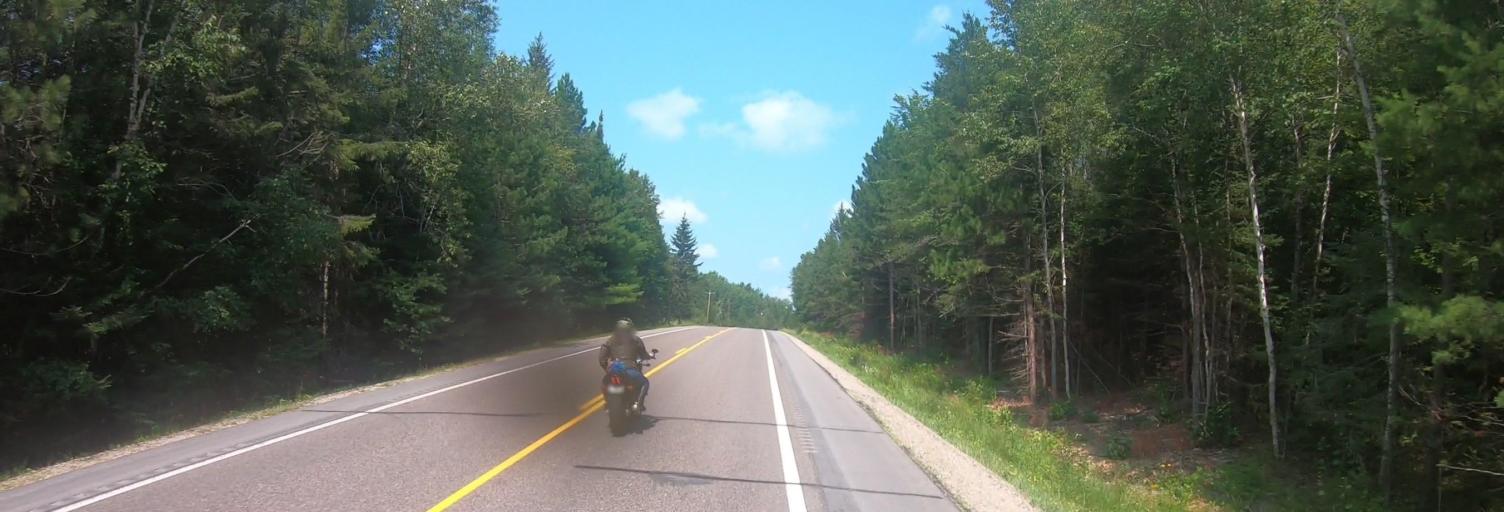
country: US
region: Minnesota
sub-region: Saint Louis County
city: Parkville
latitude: 48.1634
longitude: -92.5270
